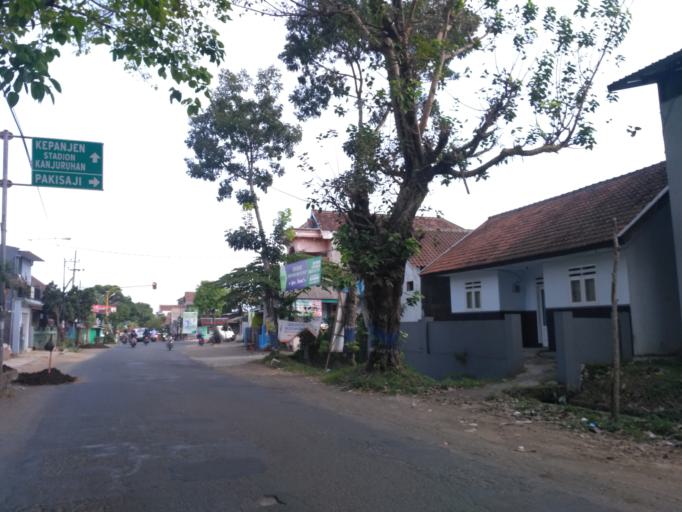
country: ID
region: East Java
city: Golek
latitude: -8.0630
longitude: 112.6267
